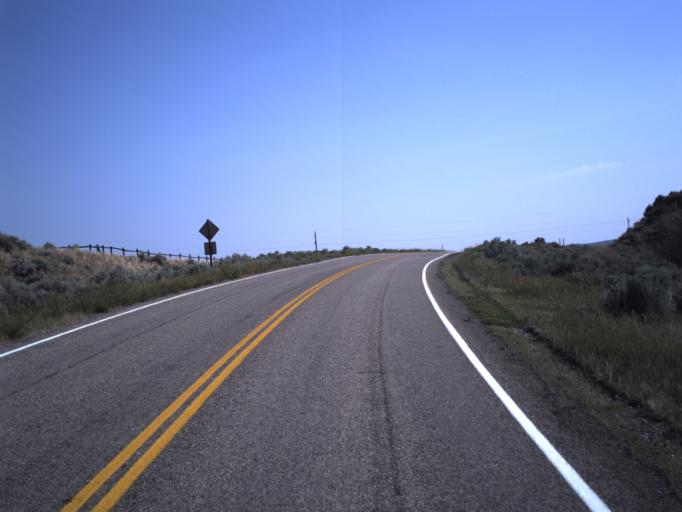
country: US
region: Utah
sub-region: Daggett County
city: Manila
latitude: 40.9565
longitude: -109.4712
